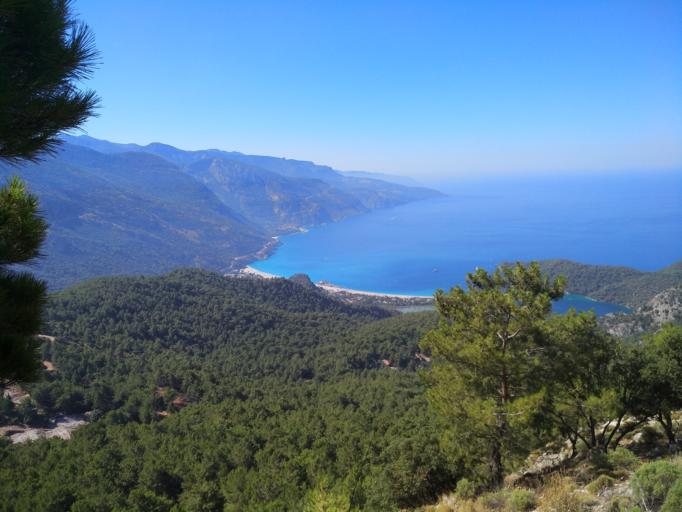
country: TR
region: Mugla
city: OEluedeniz
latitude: 36.5686
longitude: 29.1173
